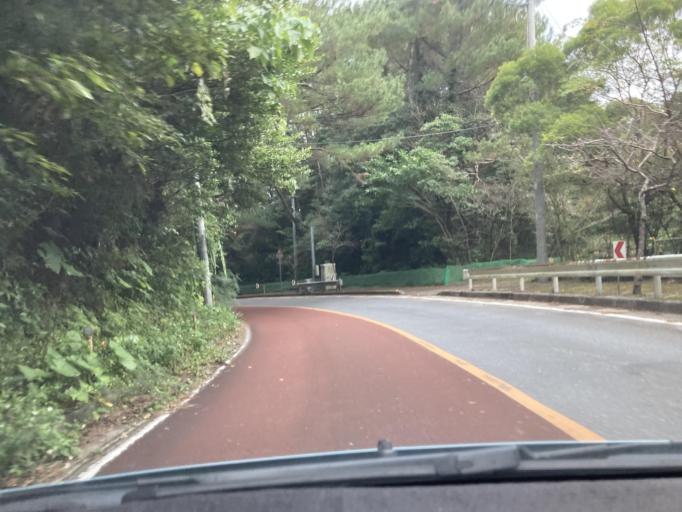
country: JP
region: Okinawa
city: Nago
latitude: 26.8308
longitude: 128.2780
